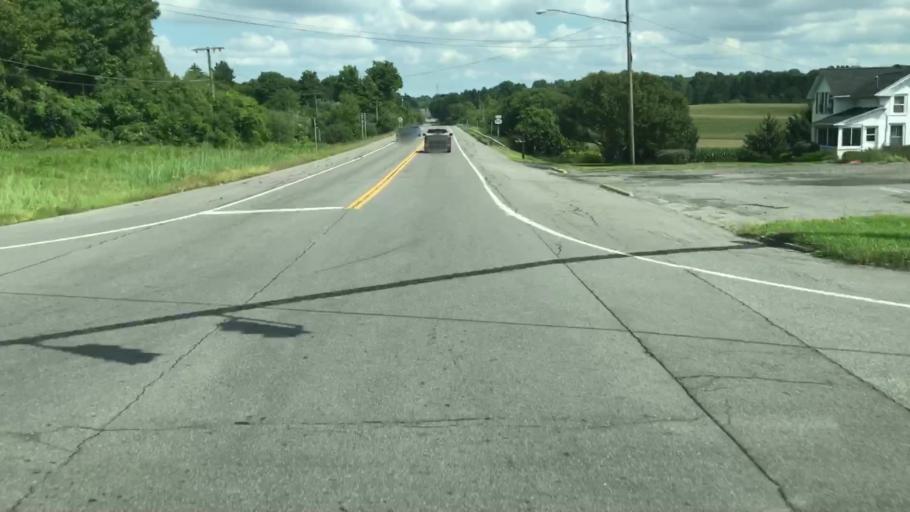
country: US
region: New York
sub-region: Onondaga County
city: Fairmount
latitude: 42.9890
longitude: -76.2503
